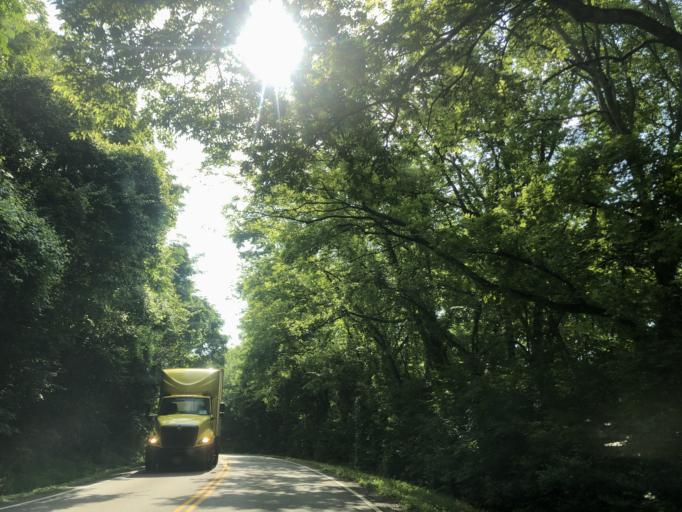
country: US
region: Tennessee
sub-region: Rutherford County
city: La Vergne
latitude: 36.1183
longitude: -86.6558
